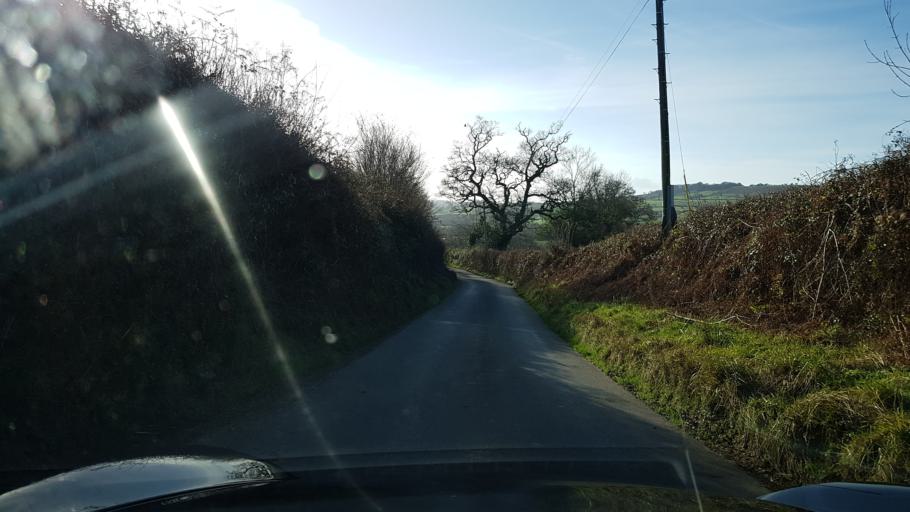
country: GB
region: England
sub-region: Dorset
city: Lyme Regis
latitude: 50.7918
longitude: -2.8713
